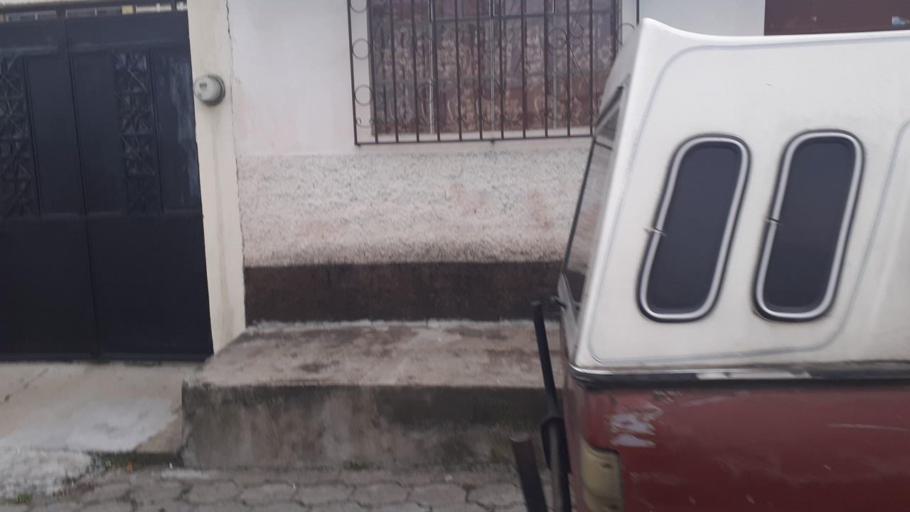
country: GT
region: Quetzaltenango
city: Quetzaltenango
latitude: 14.8404
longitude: -91.5279
